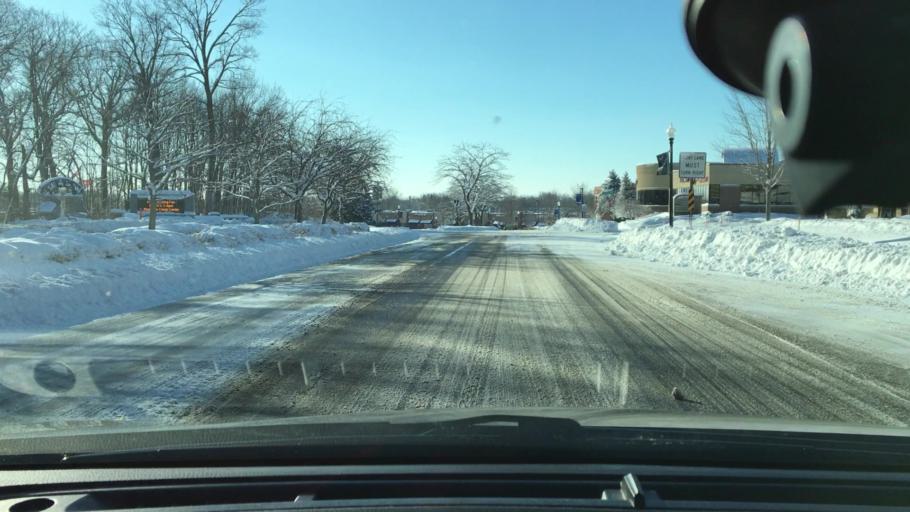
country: US
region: Minnesota
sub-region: Hennepin County
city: Plymouth
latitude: 45.0209
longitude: -93.4772
